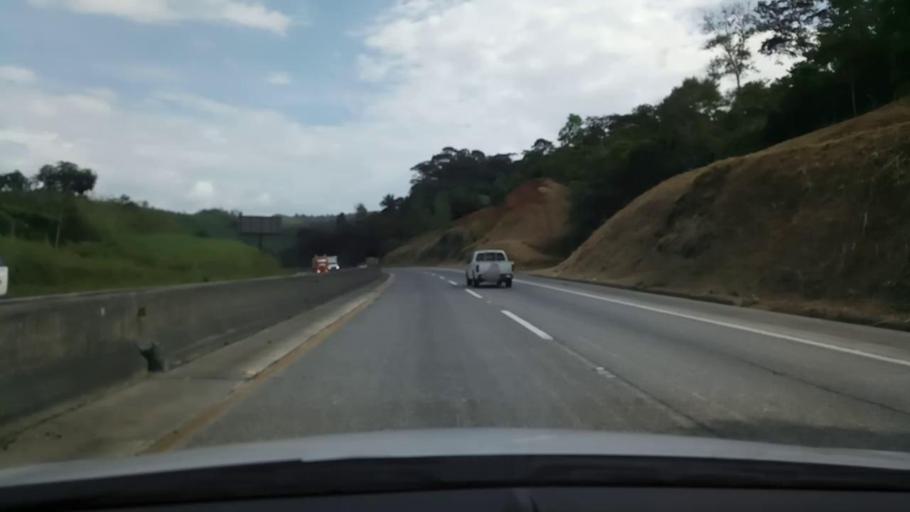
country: PA
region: Colon
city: Quebrada Bonita Adentro
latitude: 9.2771
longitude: -79.7253
